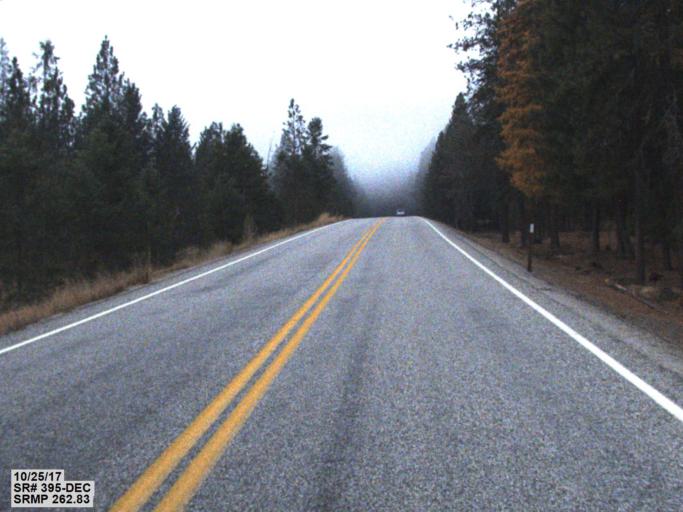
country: CA
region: British Columbia
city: Grand Forks
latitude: 48.9000
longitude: -118.2131
